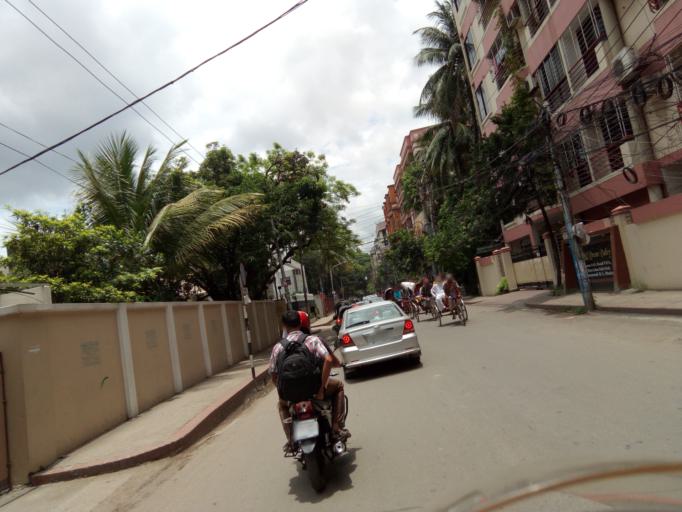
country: BD
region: Dhaka
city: Azimpur
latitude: 23.7455
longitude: 90.3750
